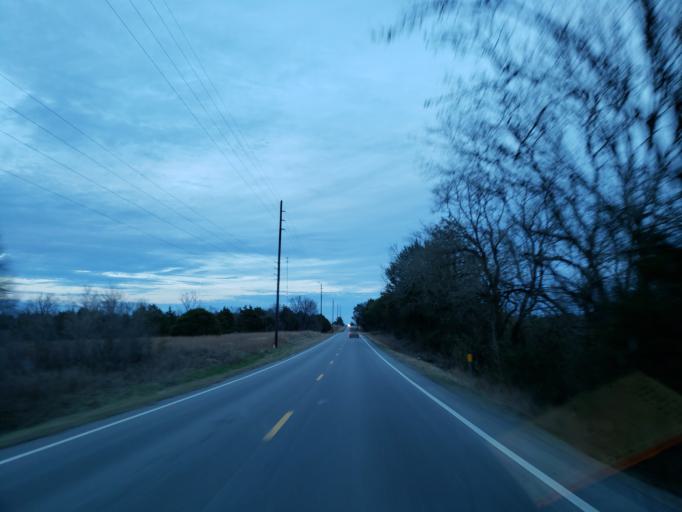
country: US
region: Alabama
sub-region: Sumter County
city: Livingston
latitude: 32.8060
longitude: -88.3020
